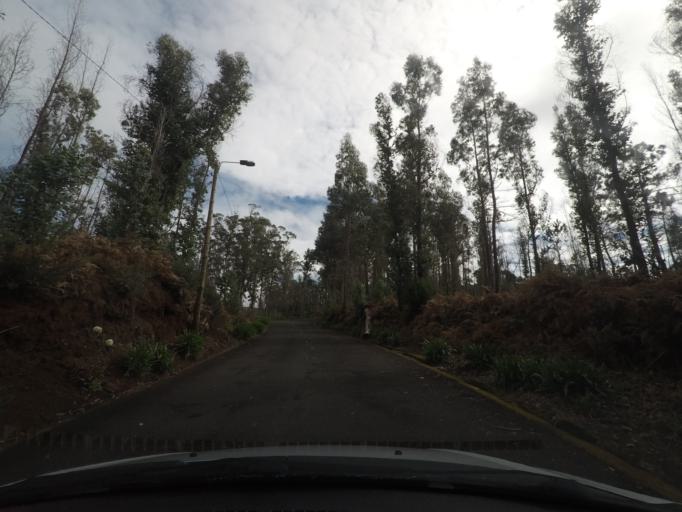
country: PT
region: Madeira
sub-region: Calheta
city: Faja da Ovelha
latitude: 32.8296
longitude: -17.2262
